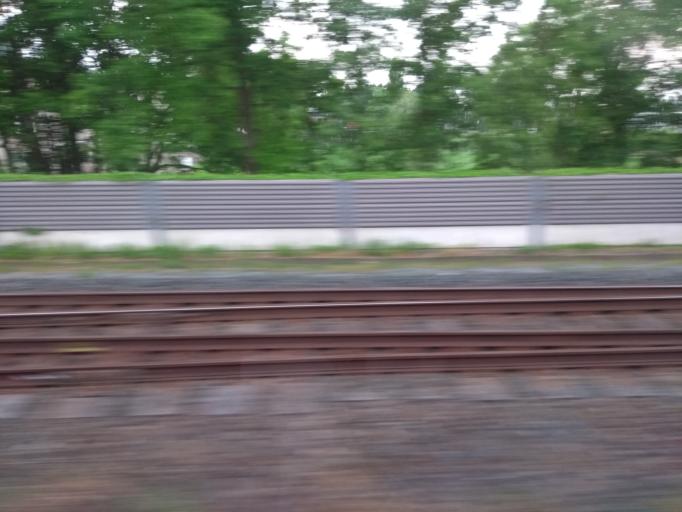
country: NL
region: North Holland
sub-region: Gemeente Weesp
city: Weesp
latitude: 52.3111
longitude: 5.0464
